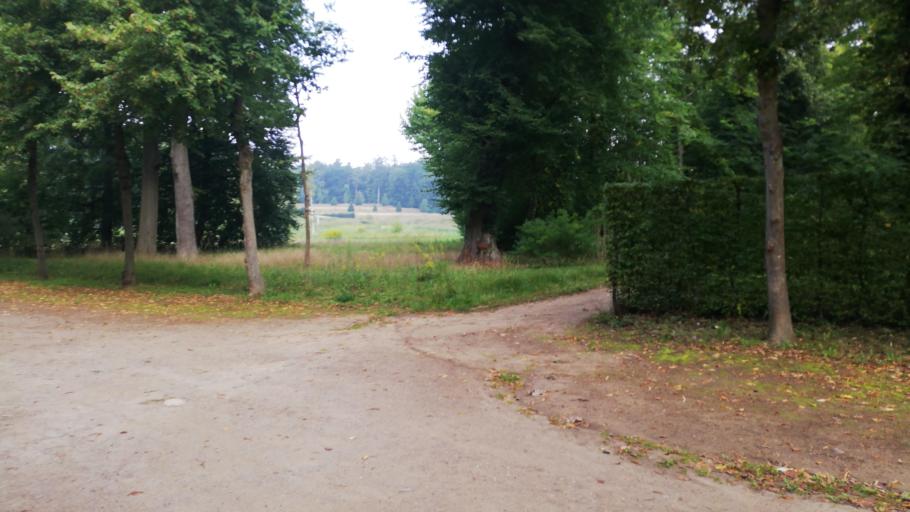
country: DE
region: Brandenburg
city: Rheinsberg
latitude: 53.0967
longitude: 12.8846
